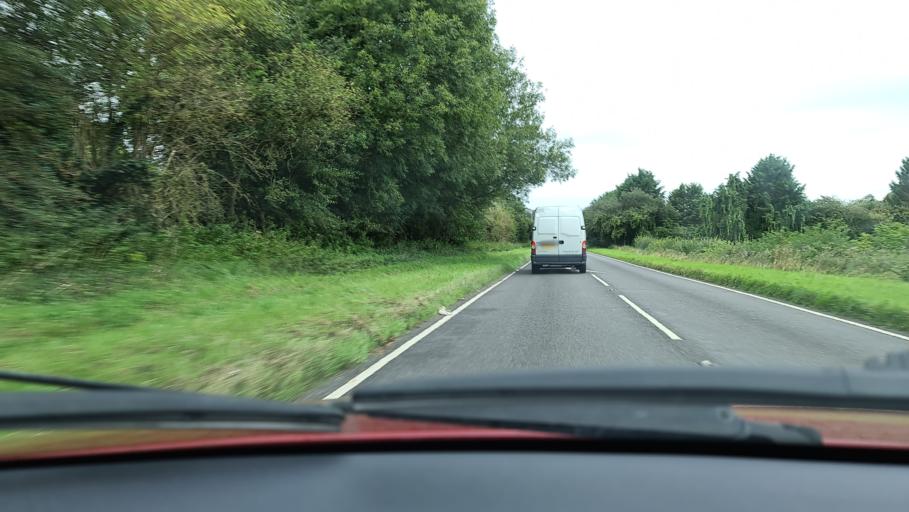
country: GB
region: England
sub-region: Buckinghamshire
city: Chesham
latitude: 51.7001
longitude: -0.6275
